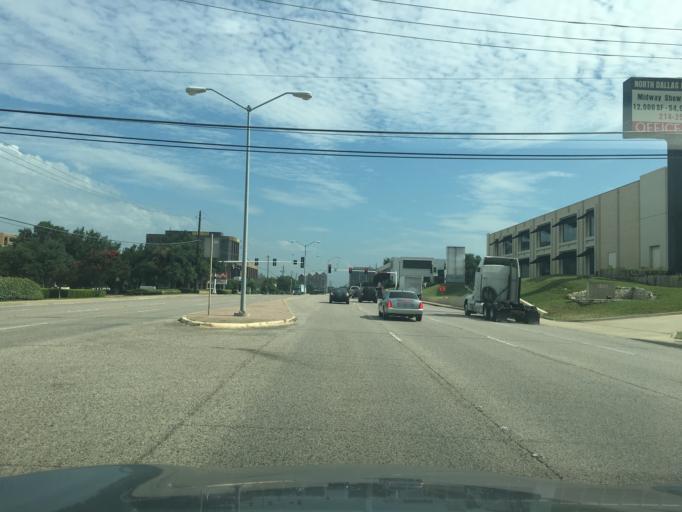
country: US
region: Texas
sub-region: Dallas County
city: Addison
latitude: 32.9276
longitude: -96.8390
